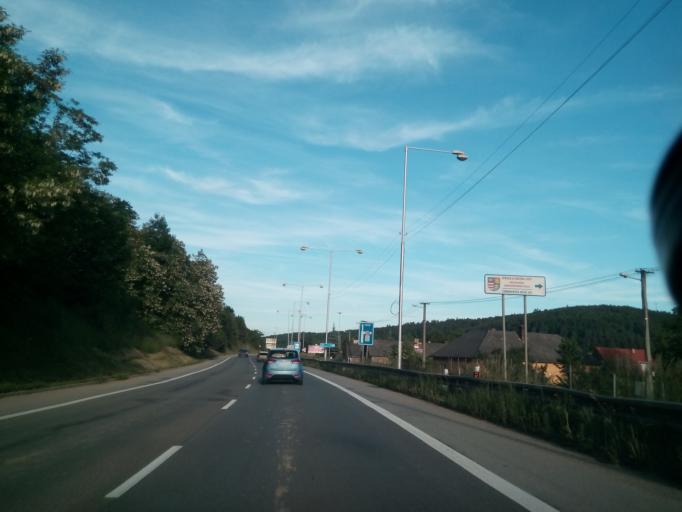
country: SK
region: Presovsky
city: Sabinov
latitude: 49.0053
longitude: 21.0727
